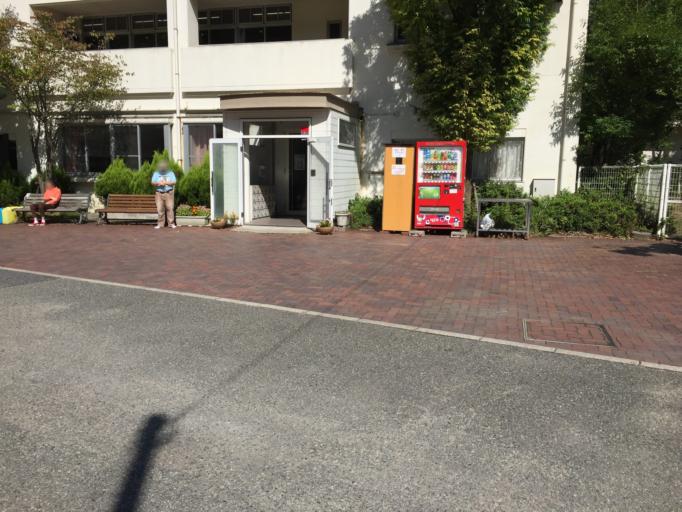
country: JP
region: Hyogo
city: Kobe
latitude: 34.7022
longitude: 135.1117
